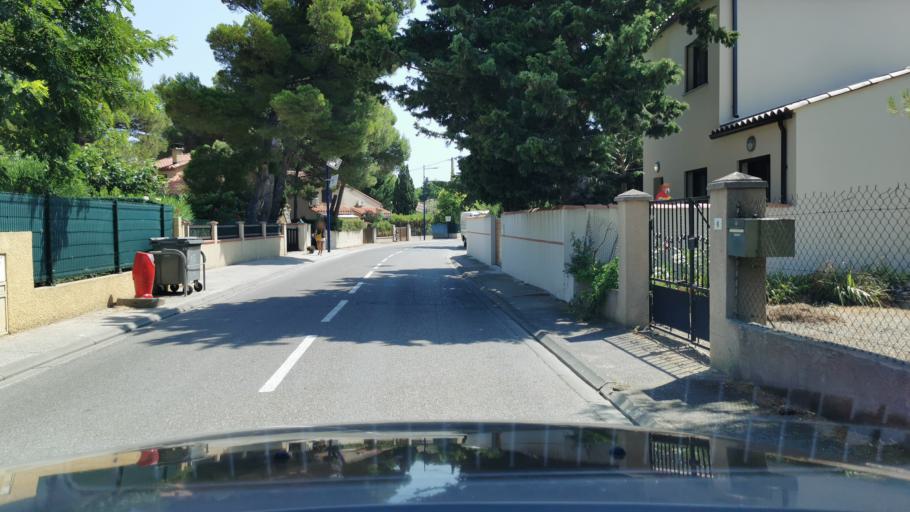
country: FR
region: Languedoc-Roussillon
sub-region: Departement de l'Aude
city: Leucate
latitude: 42.9346
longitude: 3.0283
